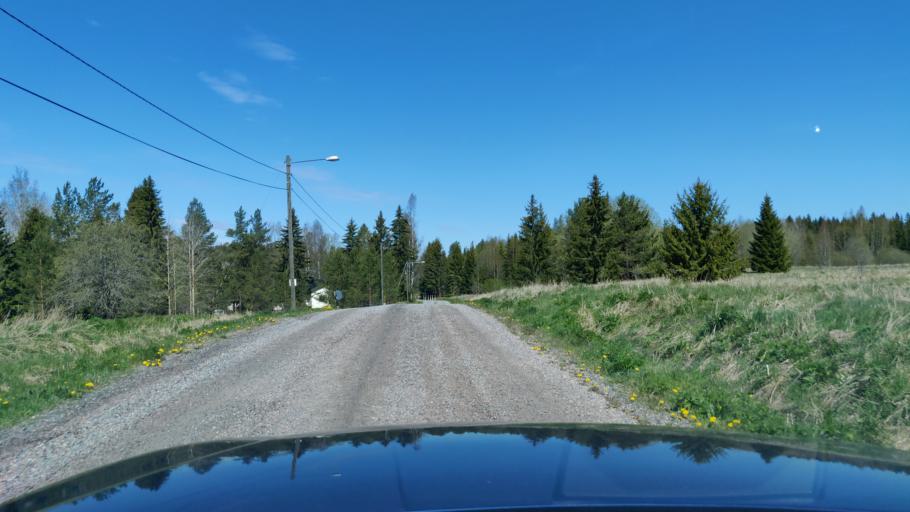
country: FI
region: Uusimaa
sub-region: Helsinki
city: Nurmijaervi
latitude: 60.3578
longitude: 24.7569
